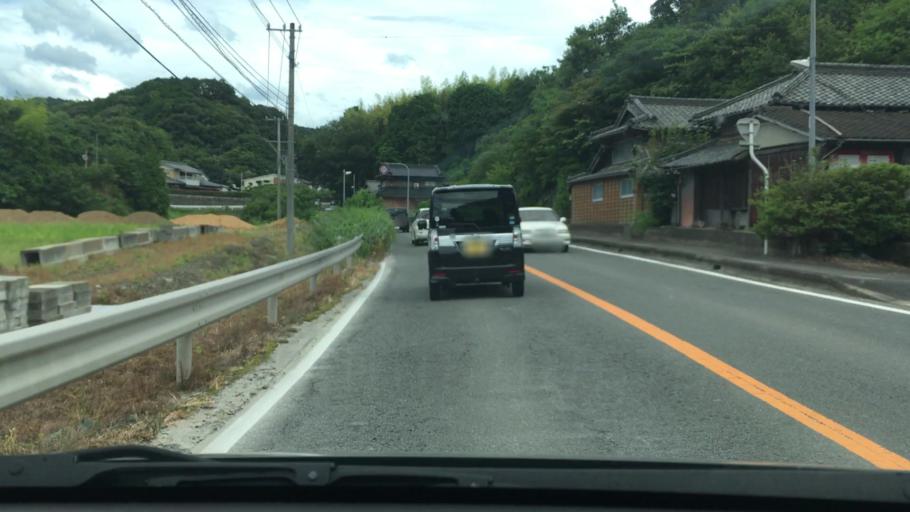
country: JP
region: Nagasaki
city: Togitsu
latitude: 32.9840
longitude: 129.7791
